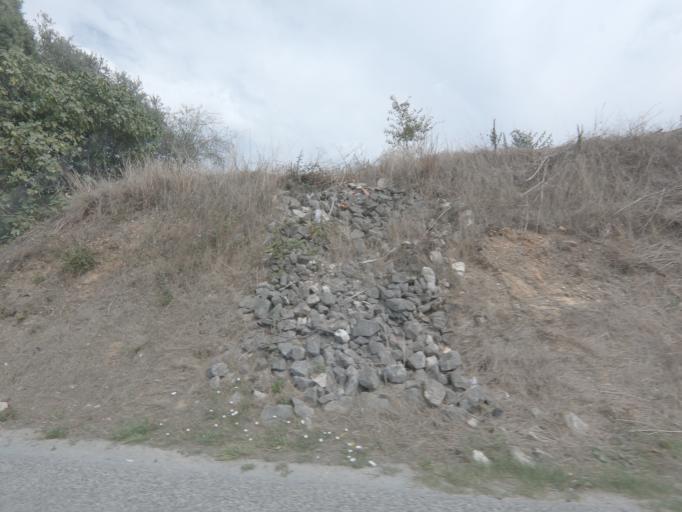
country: PT
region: Leiria
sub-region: Pombal
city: Pombal
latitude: 39.8659
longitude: -8.6960
